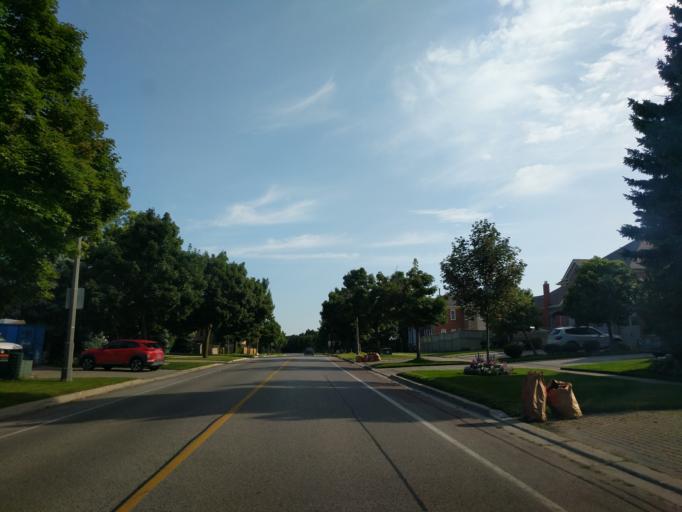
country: CA
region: Ontario
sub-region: York
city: Richmond Hill
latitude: 43.8680
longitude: -79.4009
